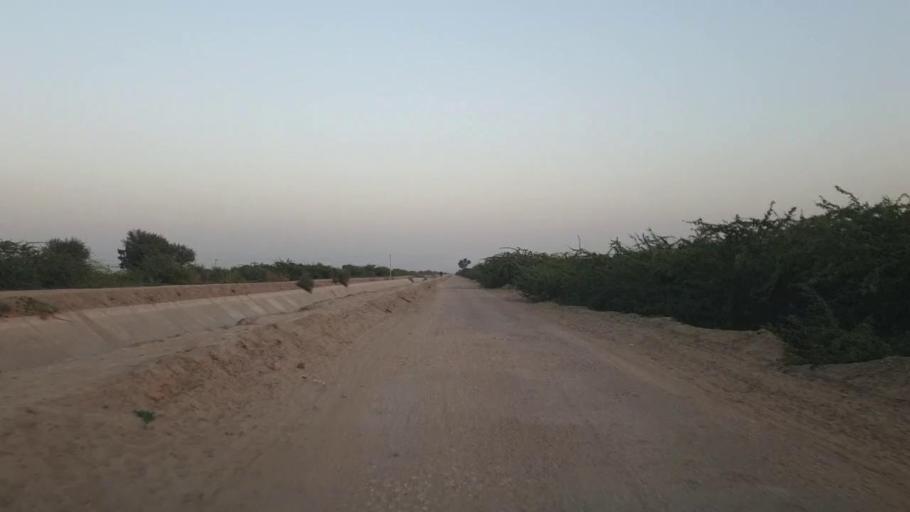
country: PK
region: Sindh
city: Umarkot
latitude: 25.4307
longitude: 69.6517
